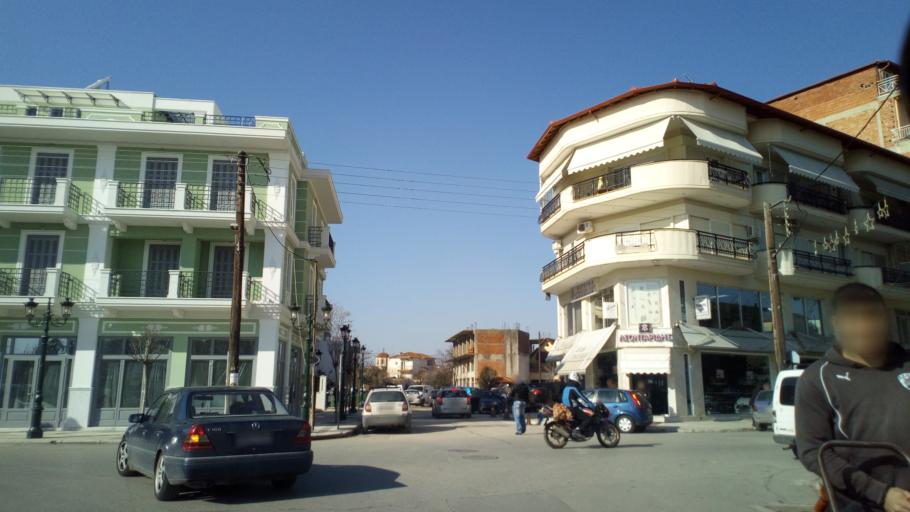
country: GR
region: Central Macedonia
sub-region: Nomos Thessalonikis
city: Lagkadas
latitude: 40.7502
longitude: 23.0668
